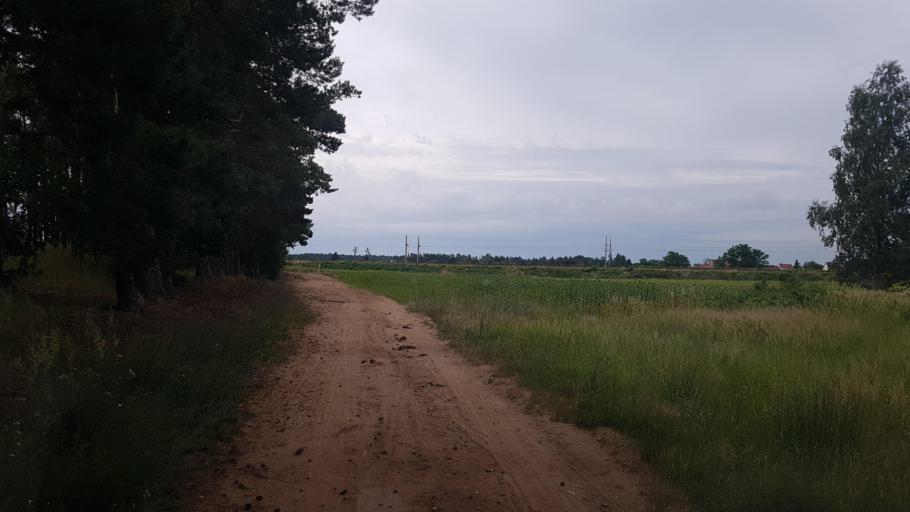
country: DE
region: Saxony-Anhalt
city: Abtsdorf
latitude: 51.8811
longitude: 12.7035
